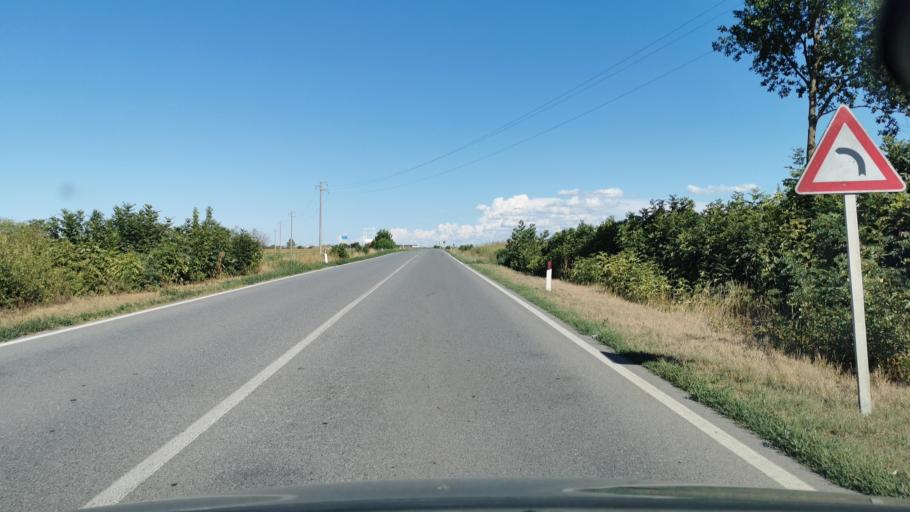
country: IT
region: Piedmont
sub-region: Provincia di Cuneo
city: Marene
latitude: 44.6564
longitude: 7.7302
